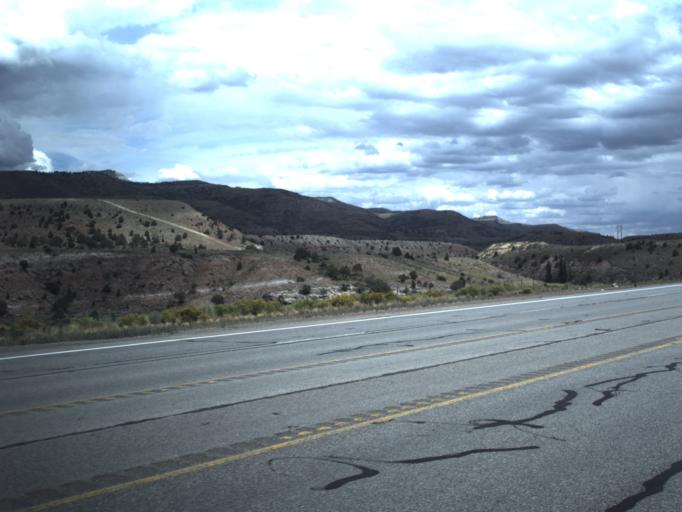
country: US
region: Utah
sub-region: Carbon County
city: Helper
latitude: 39.8353
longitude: -110.9757
